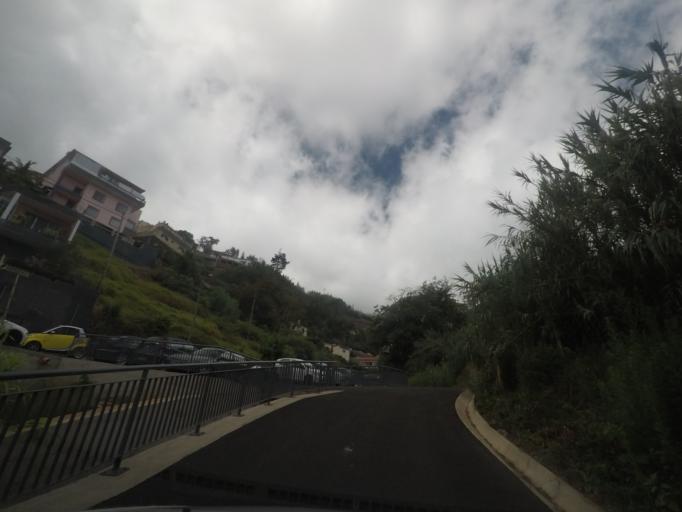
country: PT
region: Madeira
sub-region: Funchal
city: Nossa Senhora do Monte
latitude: 32.6781
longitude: -16.9092
